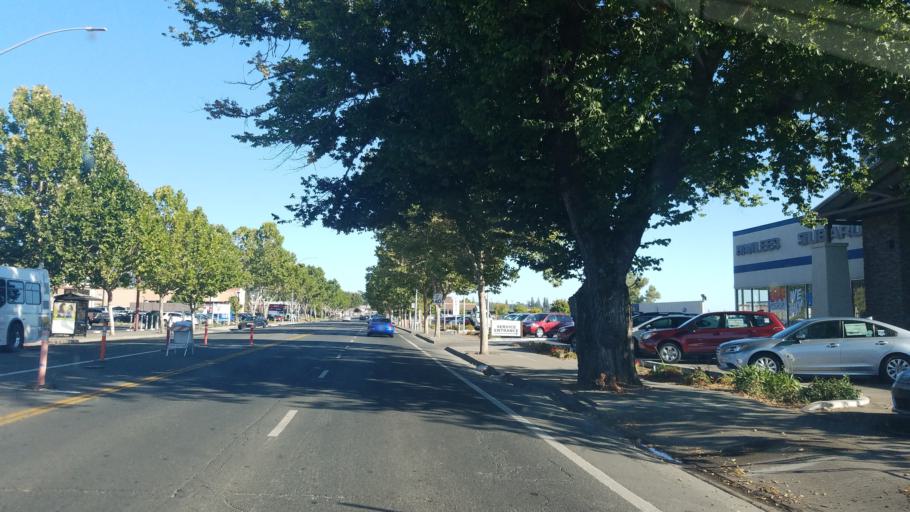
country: US
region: California
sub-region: Napa County
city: Napa
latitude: 38.2925
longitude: -122.2782
